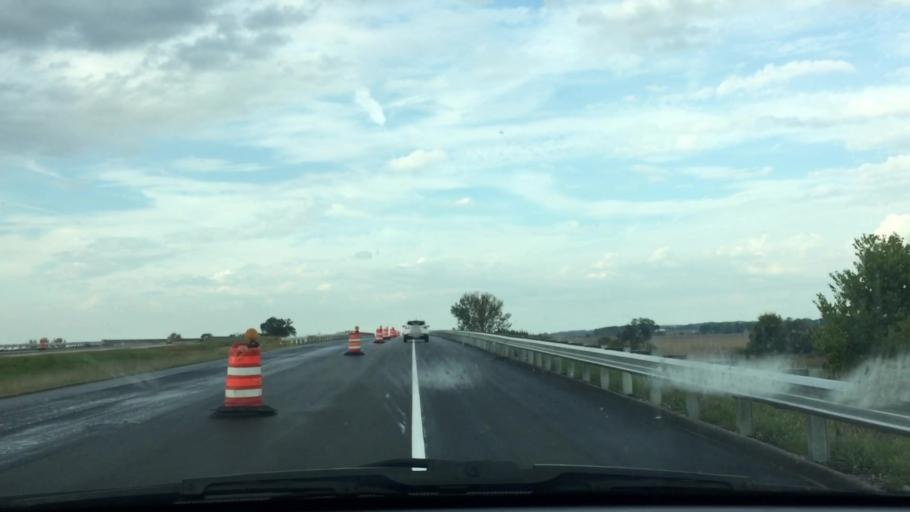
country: US
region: Illinois
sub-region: Whiteside County
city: Prophetstown
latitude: 41.7147
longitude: -90.0001
